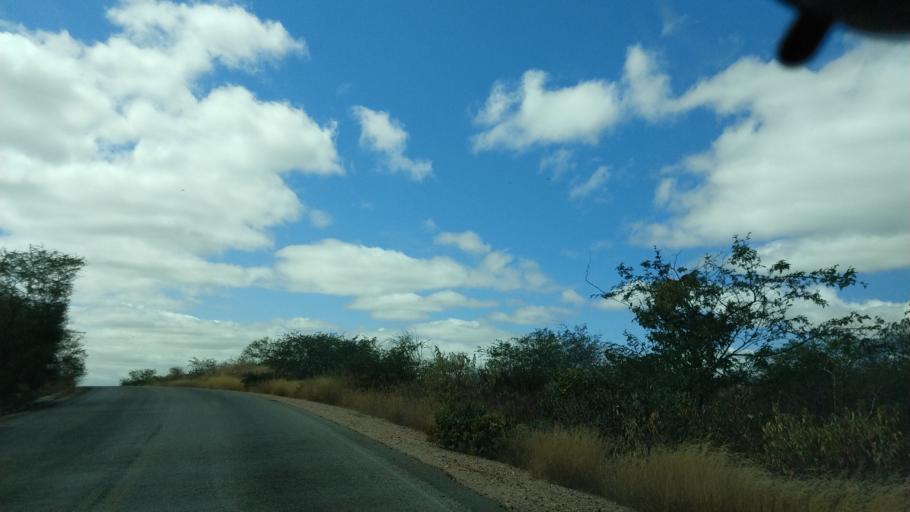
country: BR
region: Rio Grande do Norte
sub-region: Currais Novos
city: Currais Novos
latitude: -6.2700
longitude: -36.5573
